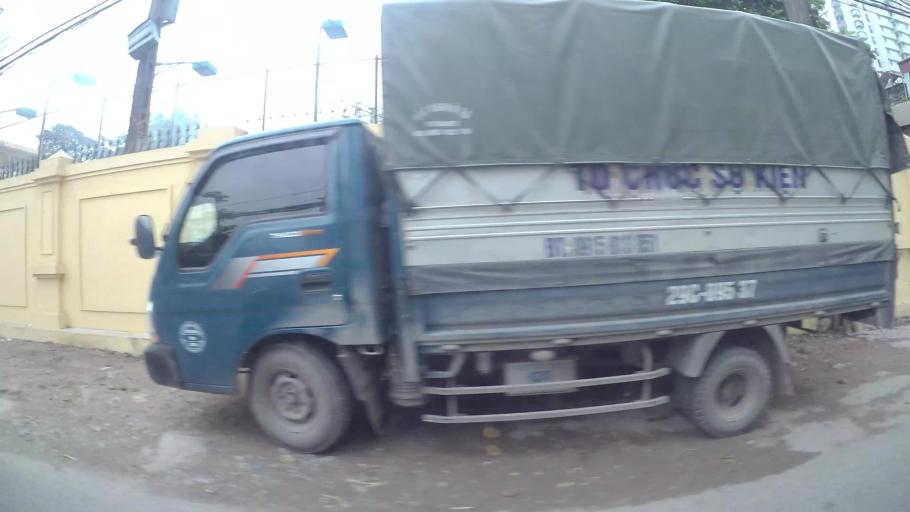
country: VN
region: Ha Noi
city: Hai BaTrung
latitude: 20.9887
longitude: 105.8661
